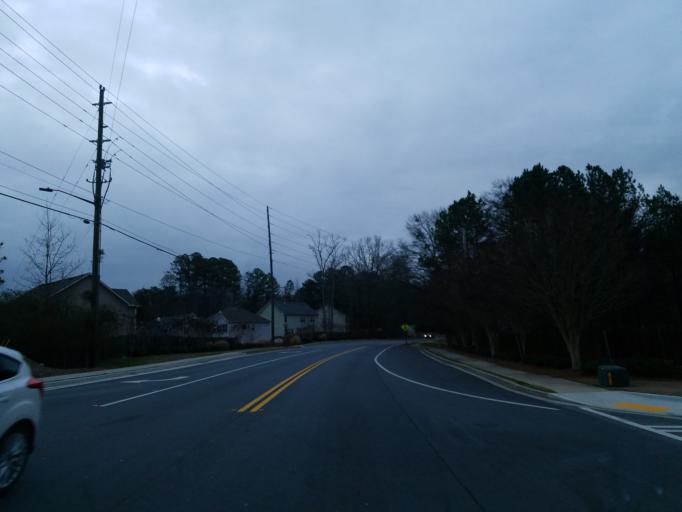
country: US
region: Georgia
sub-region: Cobb County
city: Acworth
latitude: 34.0438
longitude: -84.6557
